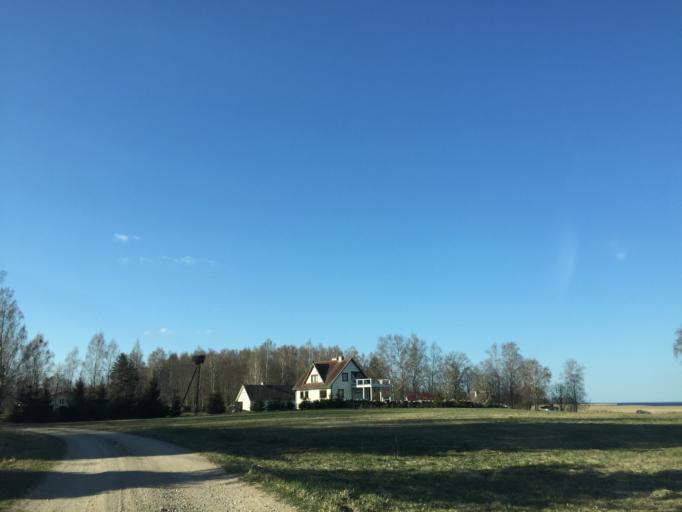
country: EE
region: Valgamaa
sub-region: Torva linn
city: Torva
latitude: 58.2272
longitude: 25.9787
